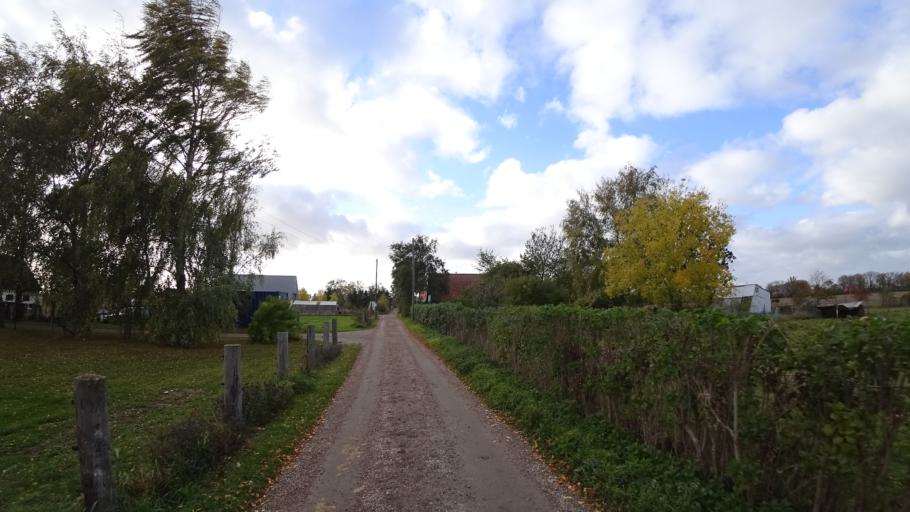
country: SE
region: Skane
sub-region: Staffanstorps Kommun
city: Staffanstorp
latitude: 55.6275
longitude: 13.2281
